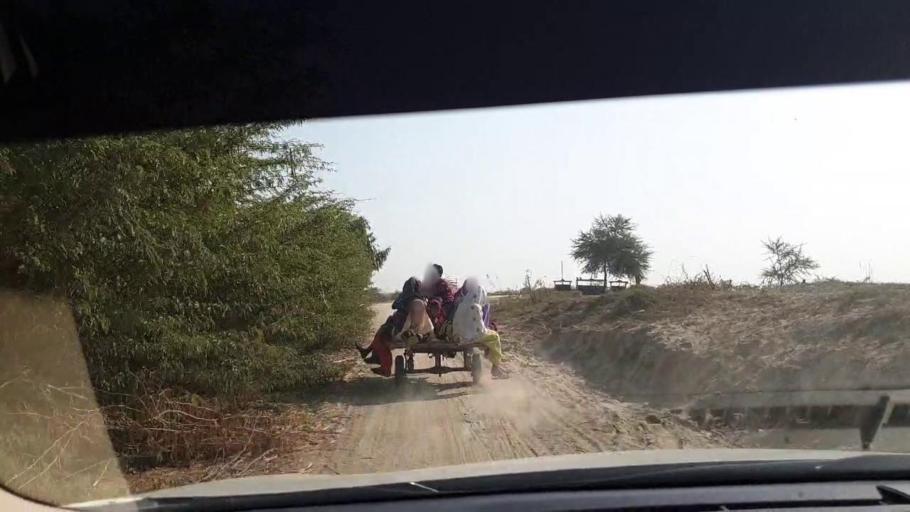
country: PK
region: Sindh
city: Tando Adam
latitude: 25.8391
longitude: 68.7228
